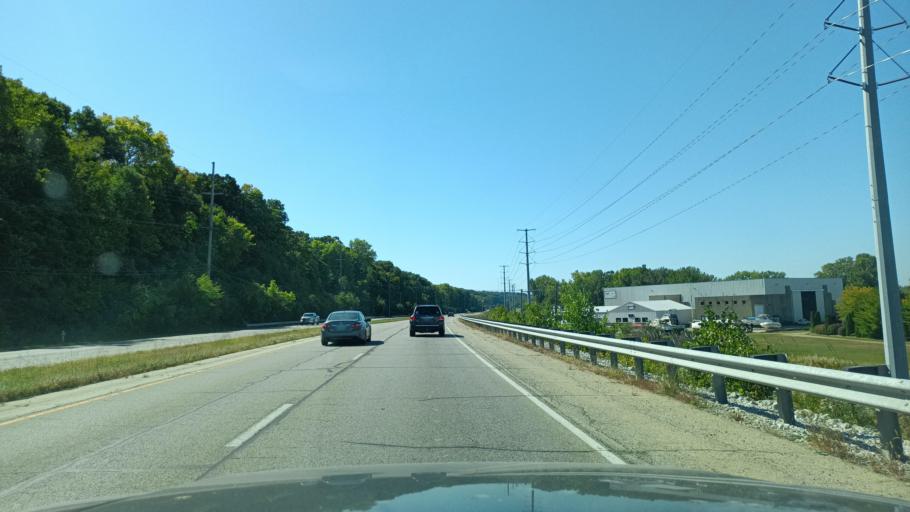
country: US
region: Illinois
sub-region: Tazewell County
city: East Peoria
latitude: 40.6926
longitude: -89.5429
